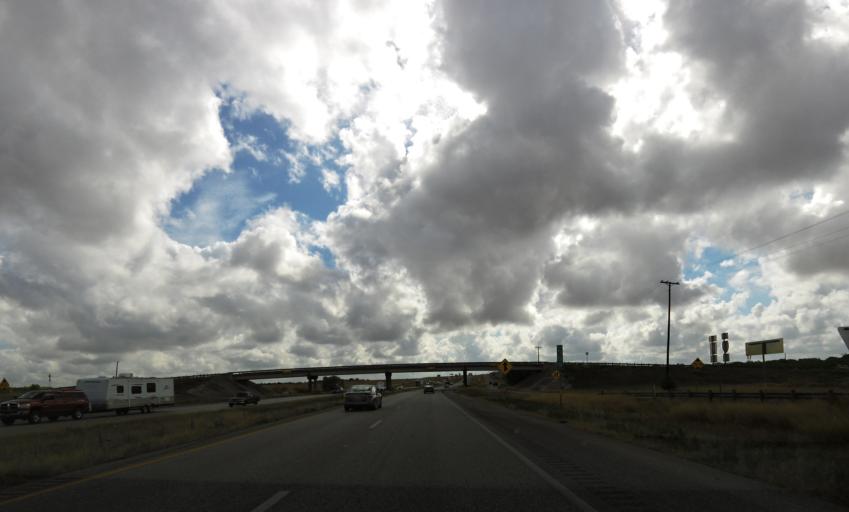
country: US
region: Texas
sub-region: Guadalupe County
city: Marion
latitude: 29.5285
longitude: -98.1136
